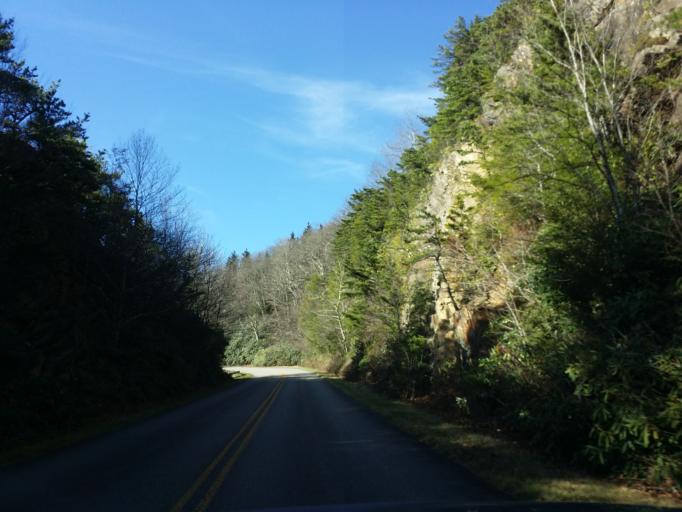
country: US
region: North Carolina
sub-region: Buncombe County
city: Black Mountain
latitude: 35.7228
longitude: -82.2130
